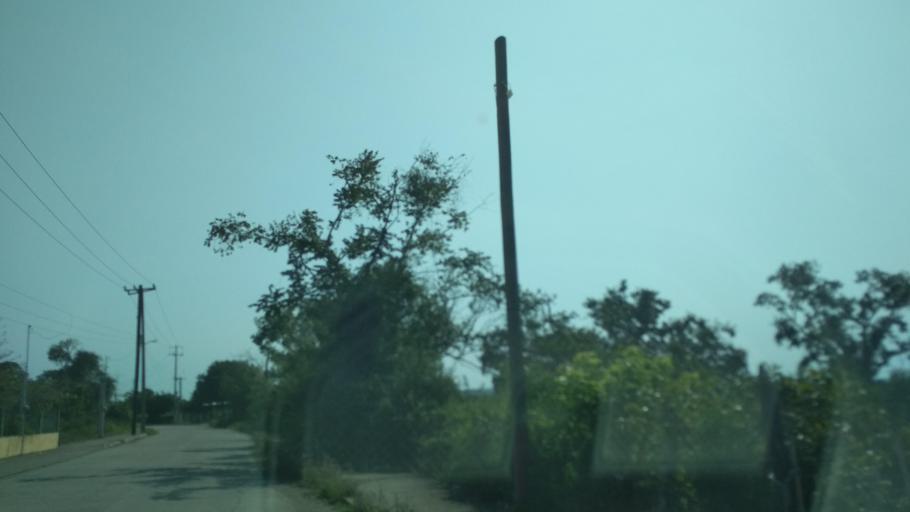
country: MX
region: Veracruz
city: Gutierrez Zamora
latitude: 20.4157
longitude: -97.1874
